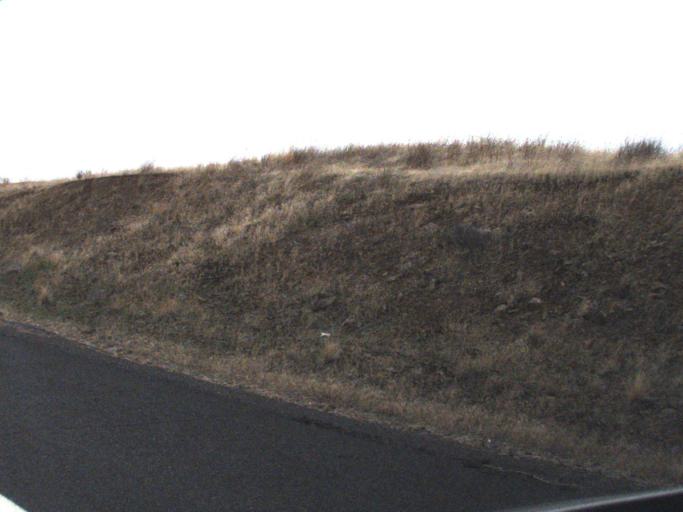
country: US
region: Washington
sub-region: Adams County
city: Ritzville
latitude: 46.7688
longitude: -118.1543
